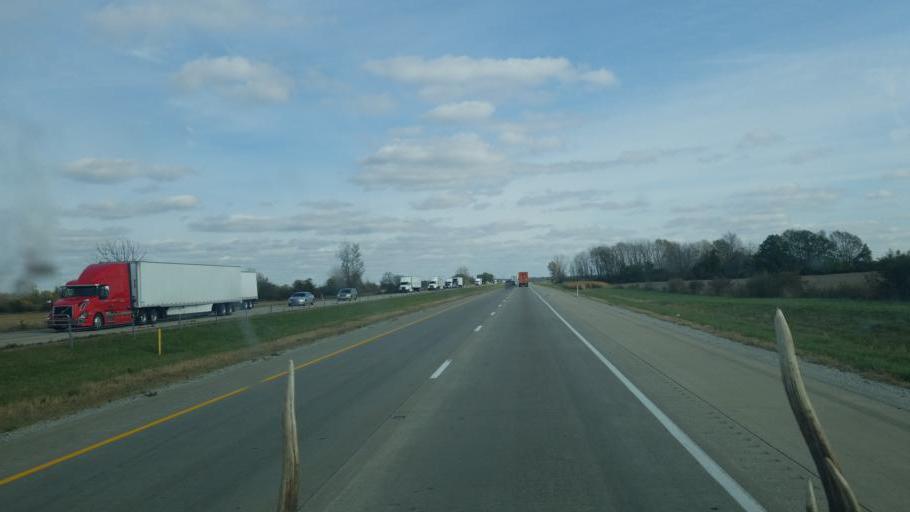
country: US
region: Indiana
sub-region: Marion County
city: Cumberland
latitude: 39.8197
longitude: -85.8723
